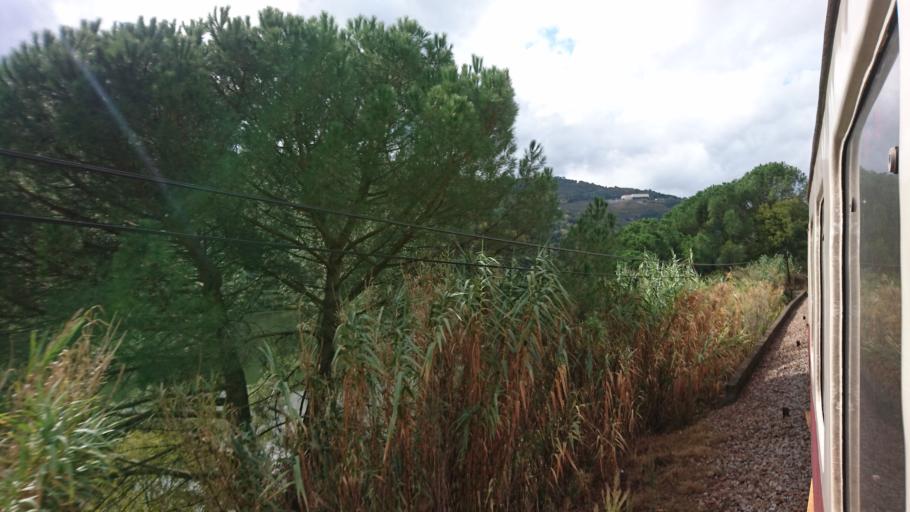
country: PT
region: Viseu
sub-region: Resende
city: Resende
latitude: 41.1215
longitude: -7.9158
